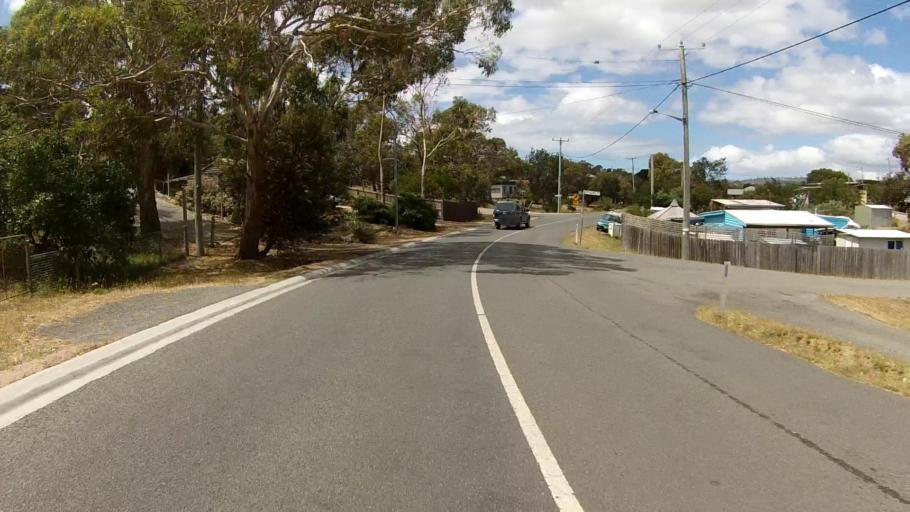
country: AU
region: Tasmania
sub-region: Sorell
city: Sorell
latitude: -42.8668
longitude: 147.6209
